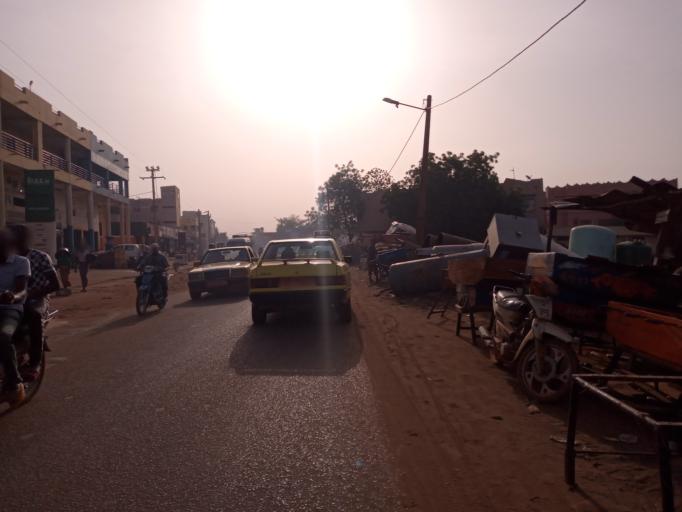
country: ML
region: Bamako
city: Bamako
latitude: 12.6630
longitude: -7.9802
